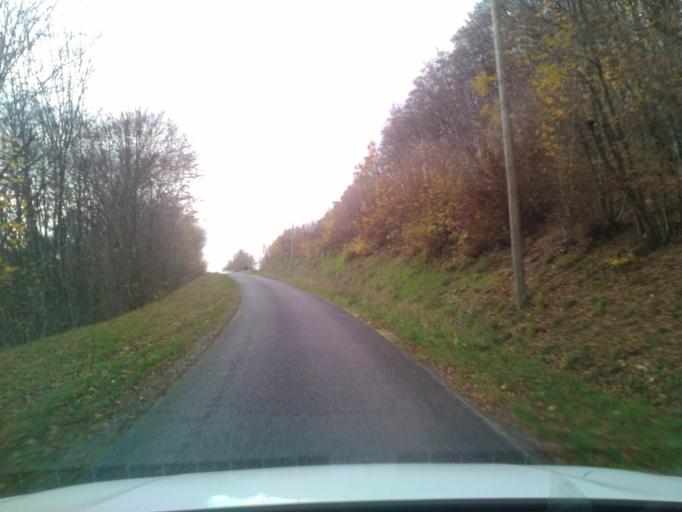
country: FR
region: Lorraine
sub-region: Departement des Vosges
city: Senones
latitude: 48.3866
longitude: 6.9435
